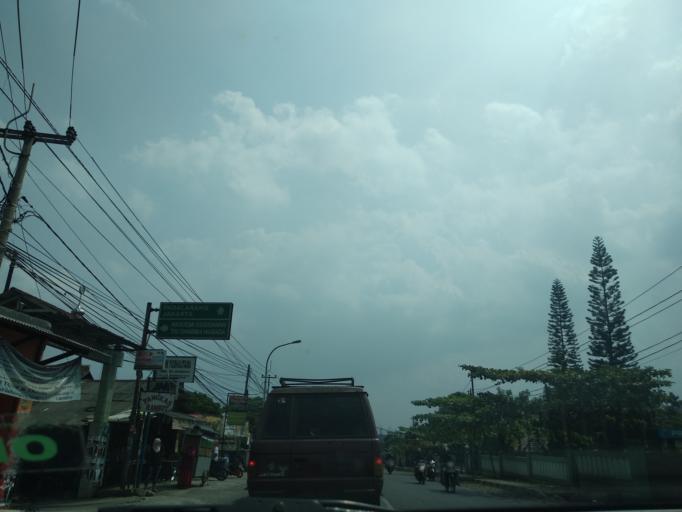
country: ID
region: West Java
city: Cimahi
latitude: -6.8651
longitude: 107.5136
